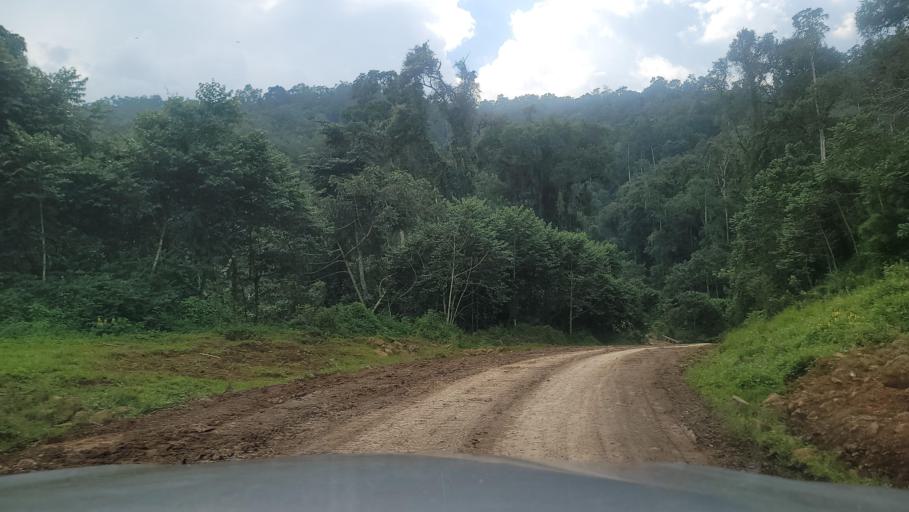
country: ET
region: Southern Nations, Nationalities, and People's Region
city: Bonga
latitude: 7.6139
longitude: 36.2051
